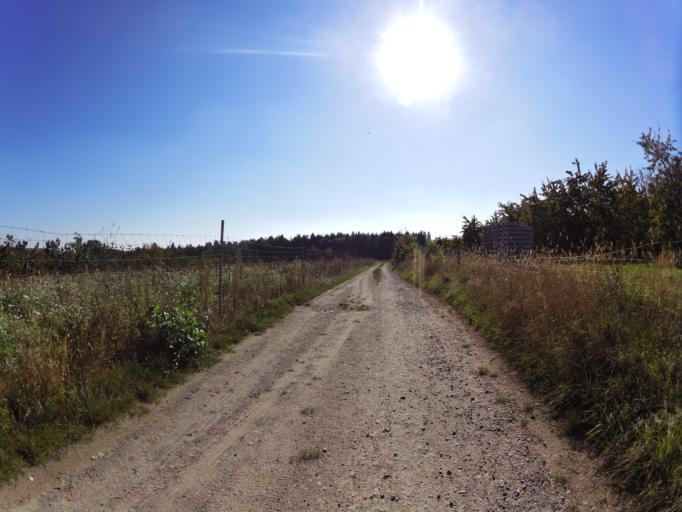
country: DE
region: Bavaria
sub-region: Regierungsbezirk Unterfranken
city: Sommerhausen
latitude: 49.6884
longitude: 10.0447
